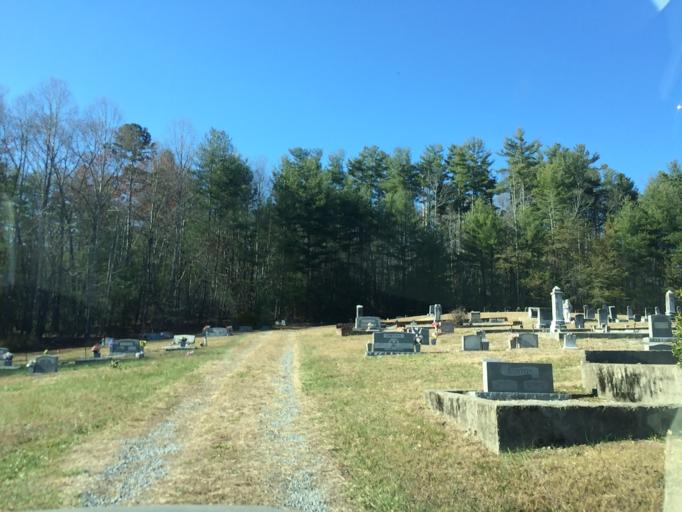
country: US
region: North Carolina
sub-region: Henderson County
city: Horse Shoe
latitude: 35.3433
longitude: -82.5349
